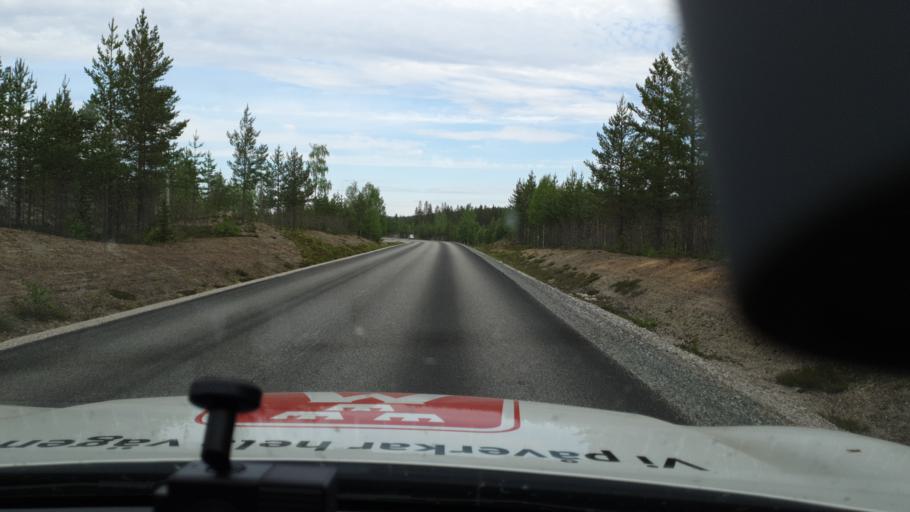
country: SE
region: Vaesterbotten
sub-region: Mala Kommun
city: Mala
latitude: 64.9662
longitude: 18.5822
